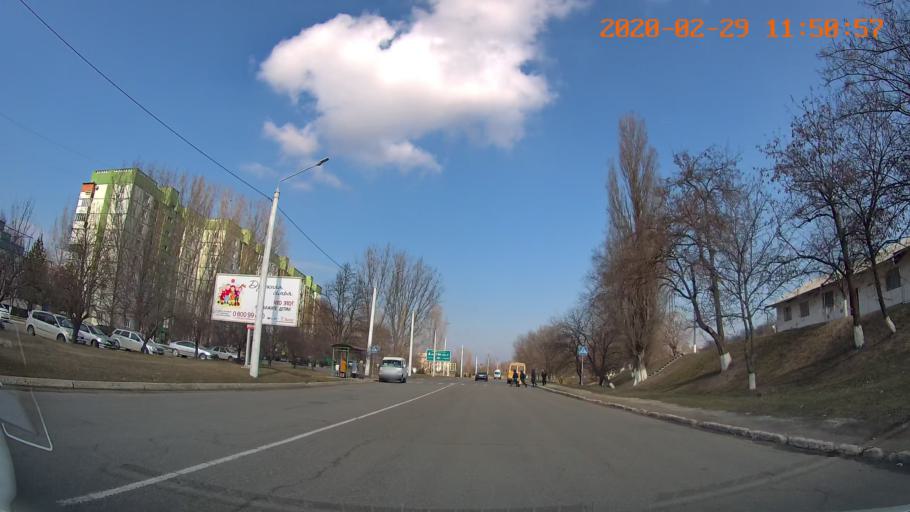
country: MD
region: Telenesti
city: Ribnita
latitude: 47.7623
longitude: 28.9896
